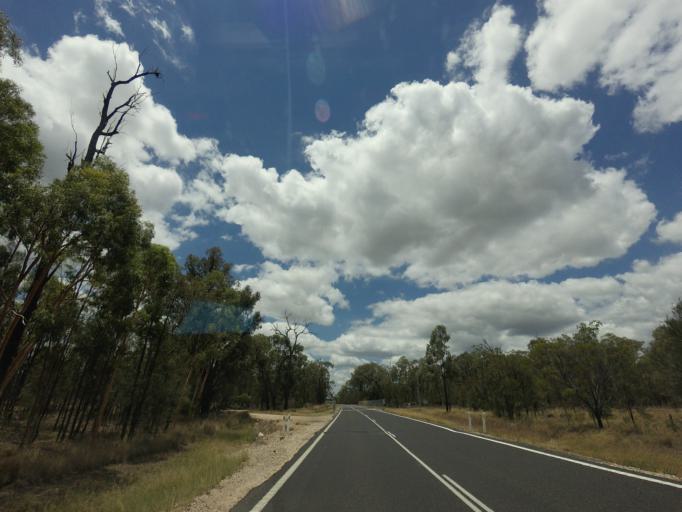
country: AU
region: Queensland
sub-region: Goondiwindi
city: Goondiwindi
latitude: -28.0306
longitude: 150.8312
